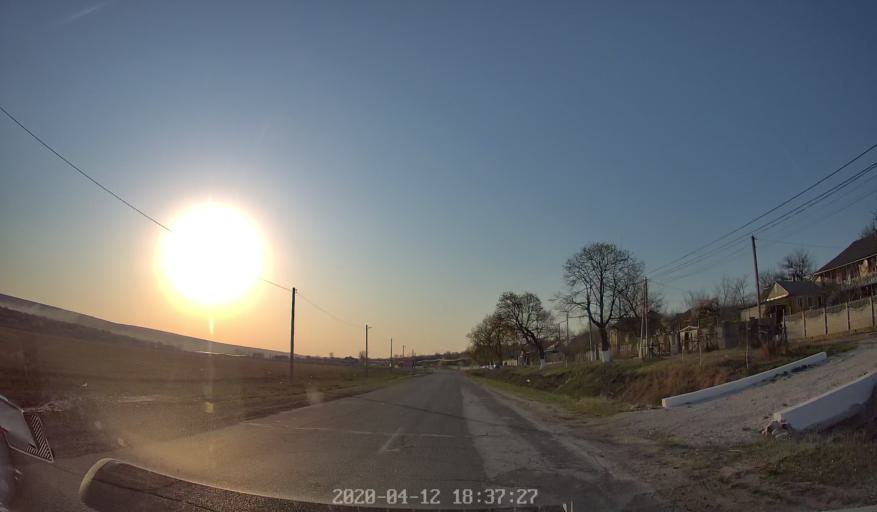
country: MD
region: Chisinau
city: Vadul lui Voda
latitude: 47.1212
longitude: 29.0152
